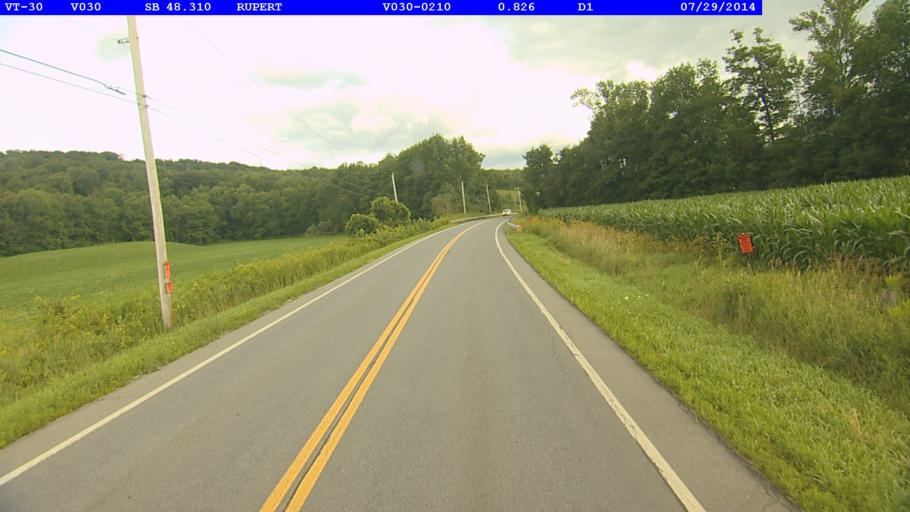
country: US
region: Vermont
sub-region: Bennington County
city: Manchester Center
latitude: 43.2822
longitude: -73.1271
